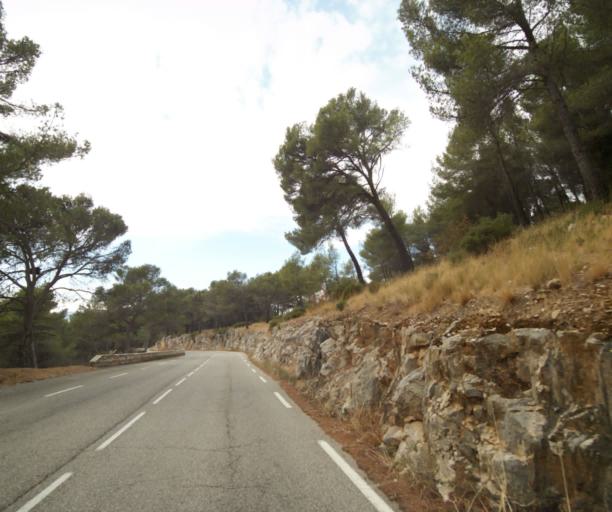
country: FR
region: Provence-Alpes-Cote d'Azur
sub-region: Departement des Bouches-du-Rhone
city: Ceyreste
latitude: 43.2296
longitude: 5.6518
